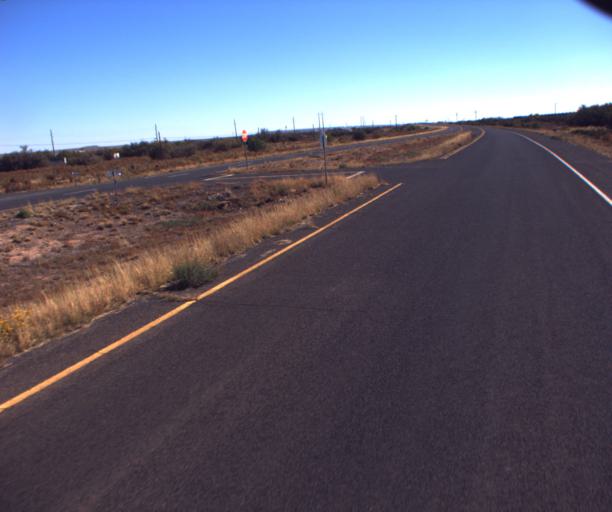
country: US
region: Arizona
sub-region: Navajo County
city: Winslow
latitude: 35.0083
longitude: -110.6623
